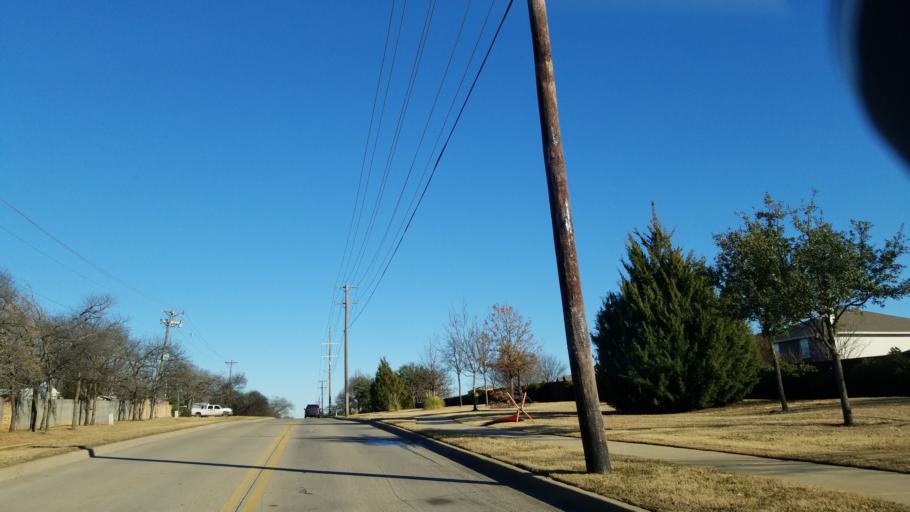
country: US
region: Texas
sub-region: Denton County
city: Corinth
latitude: 33.1583
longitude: -97.1004
